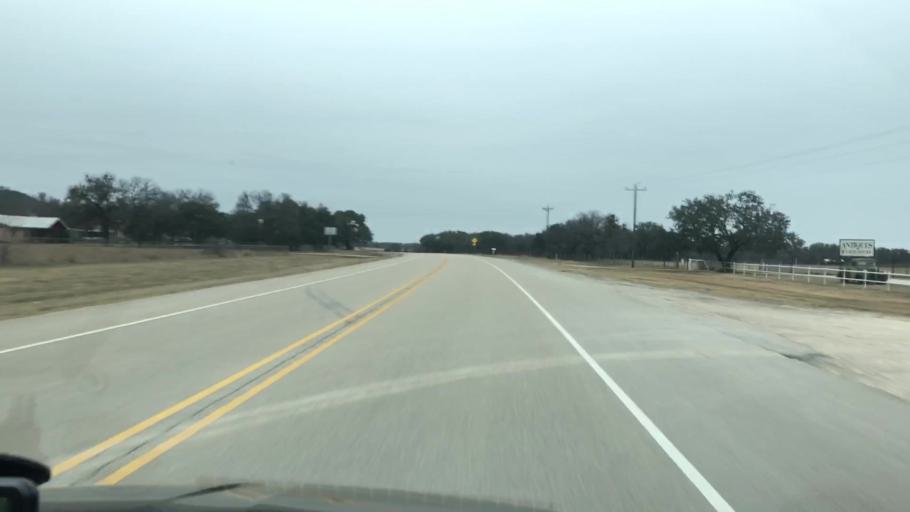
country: US
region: Texas
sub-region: Hamilton County
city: Hamilton
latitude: 31.4919
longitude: -98.1472
